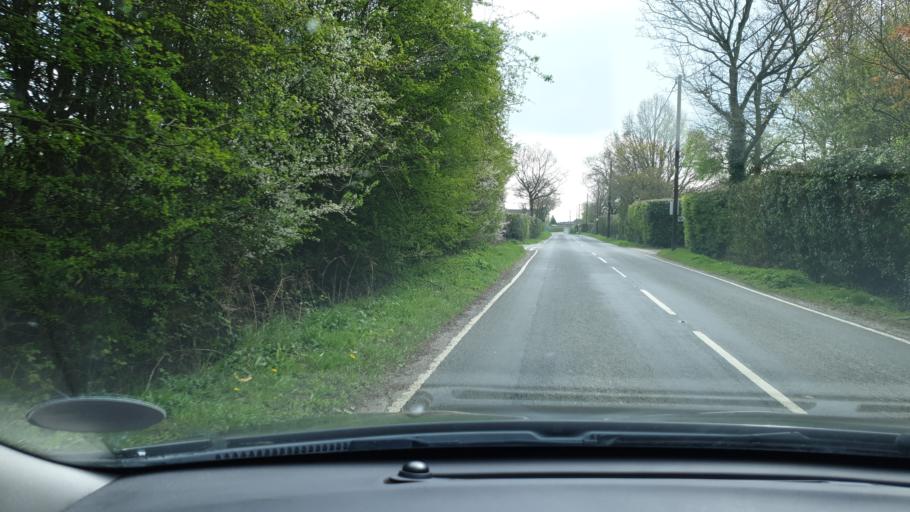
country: GB
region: England
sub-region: Essex
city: Alresford
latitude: 51.9099
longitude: 1.0023
